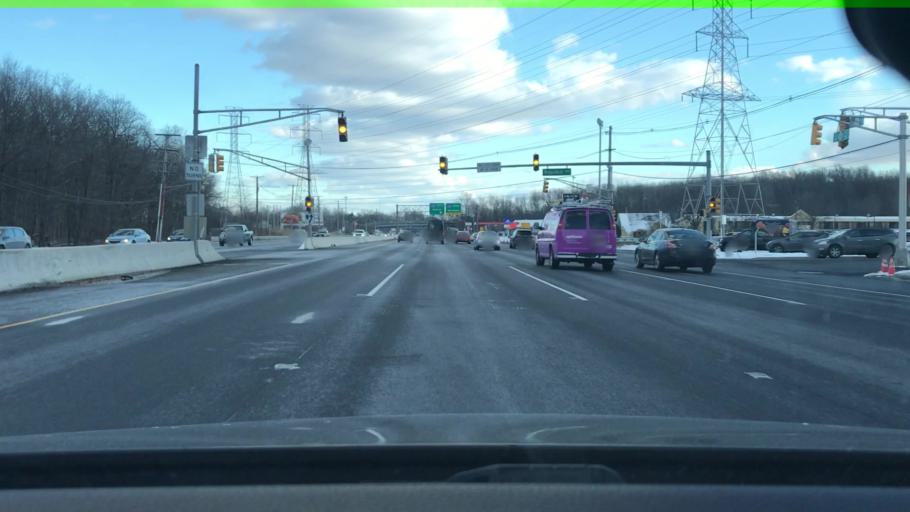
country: US
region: New Jersey
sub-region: Morris County
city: Parsippany
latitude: 40.8358
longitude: -74.4455
